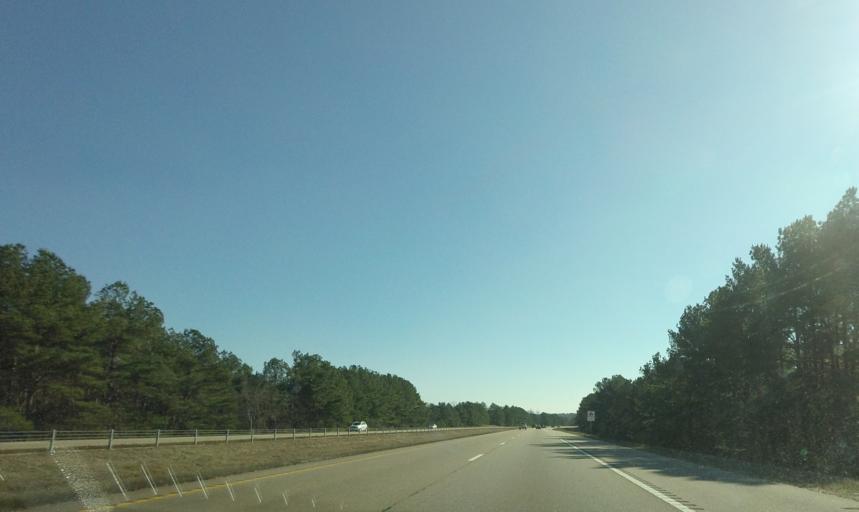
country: US
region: Mississippi
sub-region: Marshall County
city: Holly Springs
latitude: 34.7777
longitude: -89.4744
